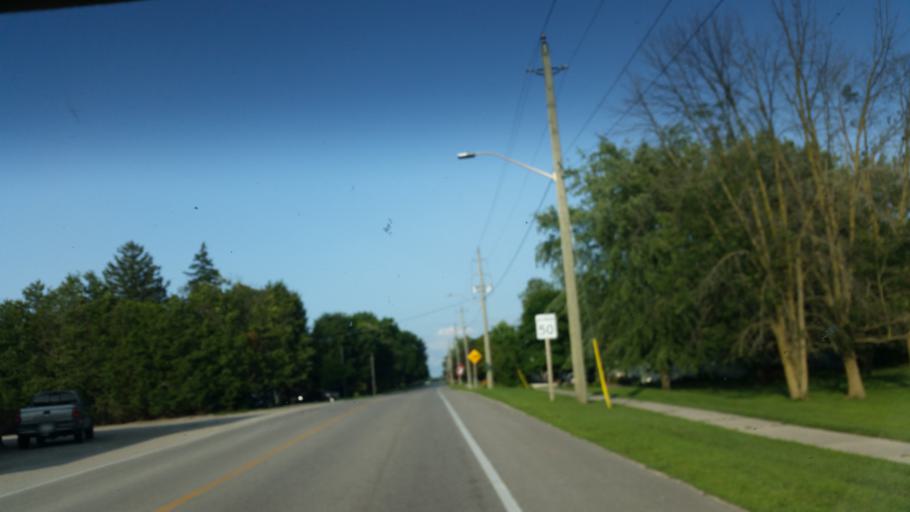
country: CA
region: Ontario
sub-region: Oxford County
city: Woodstock
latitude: 43.0238
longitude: -80.6527
